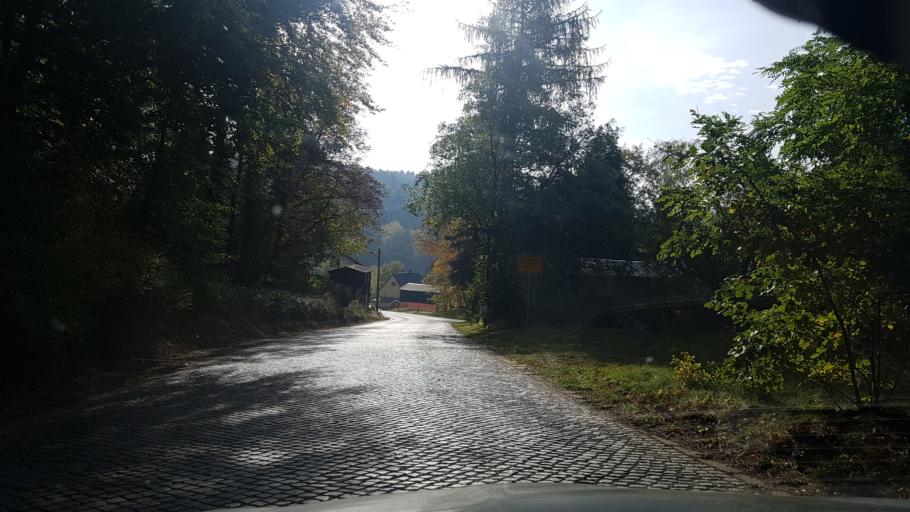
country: DE
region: Saxony
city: Struppen
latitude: 50.9072
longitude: 14.0277
